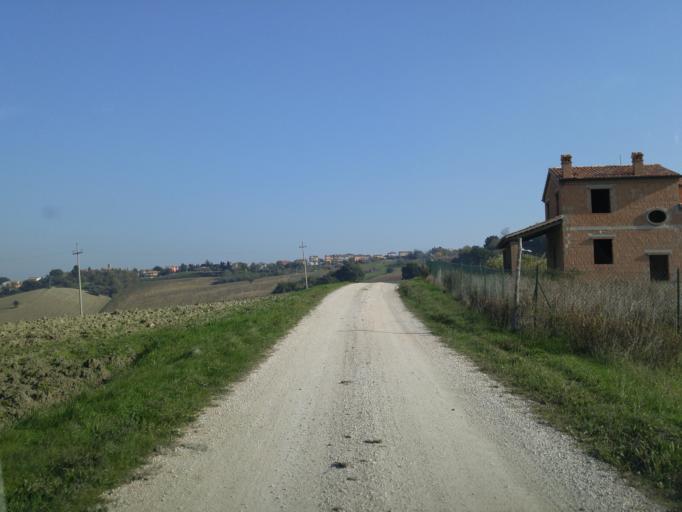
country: IT
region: The Marches
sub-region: Provincia di Pesaro e Urbino
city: Montemaggiore al Metauro
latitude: 43.7314
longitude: 12.9545
